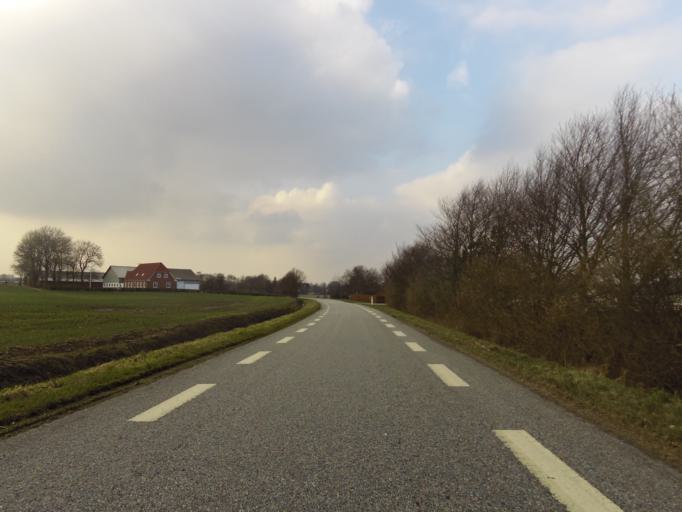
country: DK
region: South Denmark
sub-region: Haderslev Kommune
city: Gram
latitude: 55.2406
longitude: 8.9755
